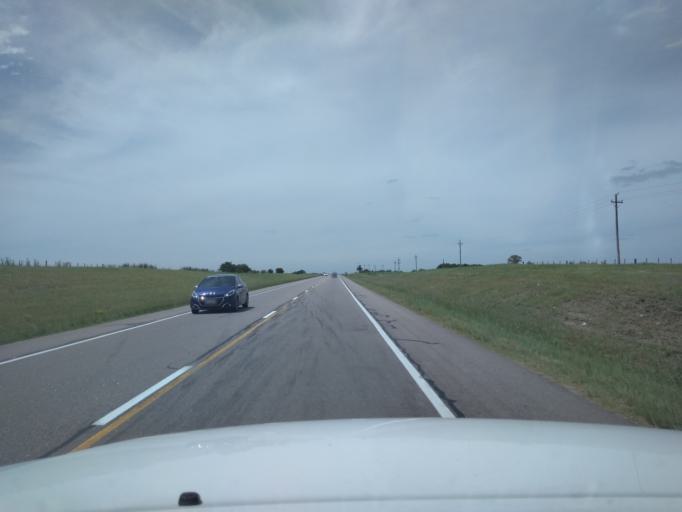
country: UY
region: Florida
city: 25 de Mayo
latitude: -34.2306
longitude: -56.2126
